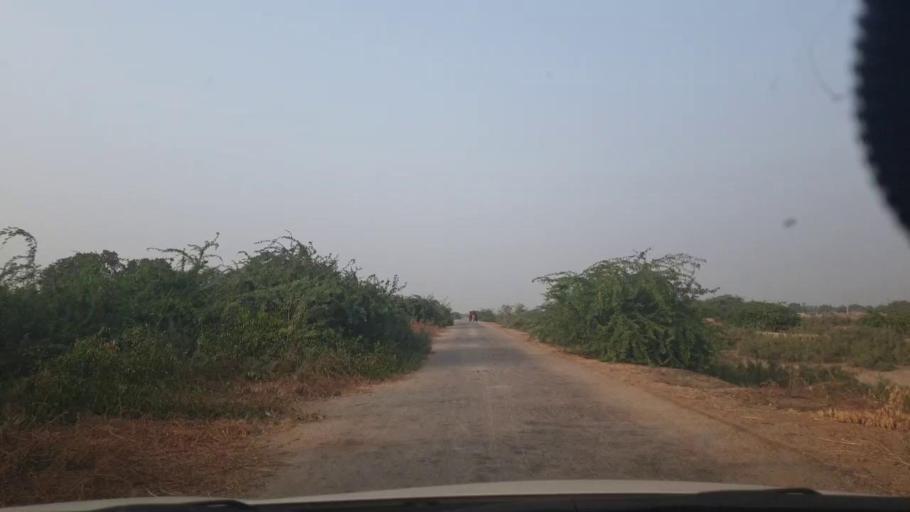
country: PK
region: Sindh
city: Bulri
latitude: 24.8239
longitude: 68.4032
